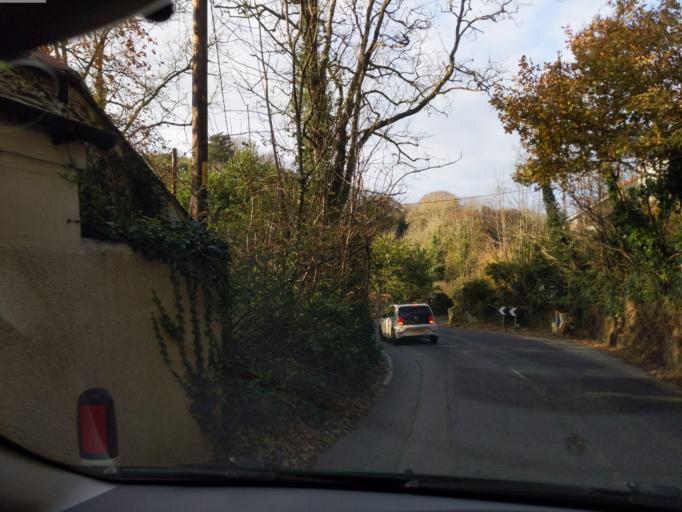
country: GB
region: England
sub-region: Cornwall
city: Padstow
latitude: 50.5119
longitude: -4.9359
